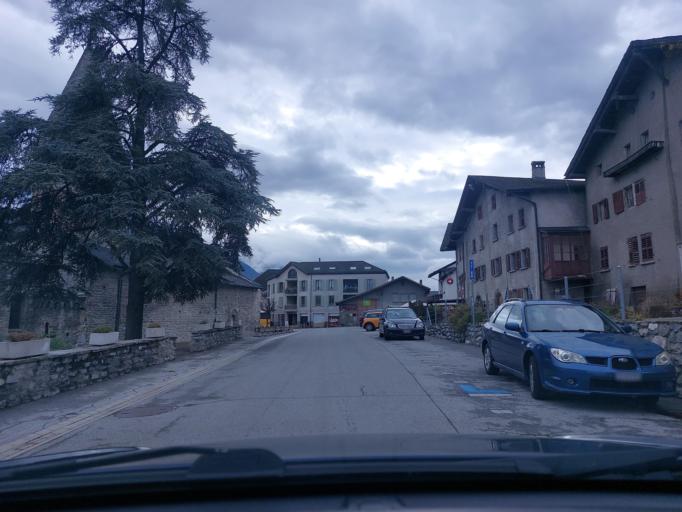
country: CH
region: Valais
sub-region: Conthey District
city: Chamoson
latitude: 46.1926
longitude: 7.2375
